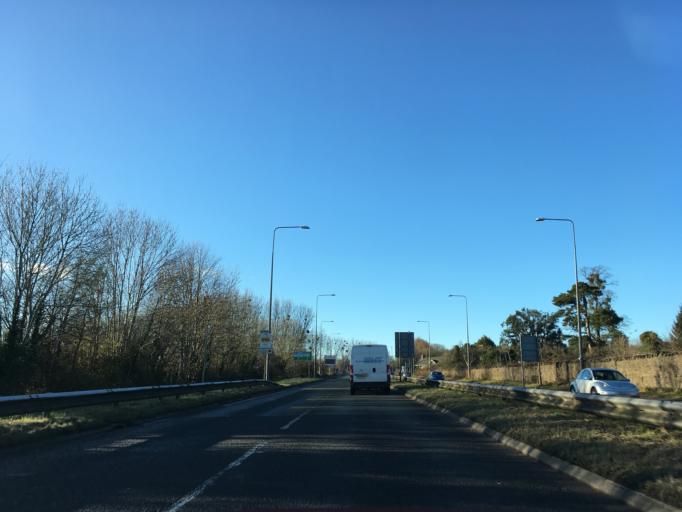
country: GB
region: England
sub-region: Bath and North East Somerset
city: Keynsham
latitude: 51.4260
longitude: -2.5228
